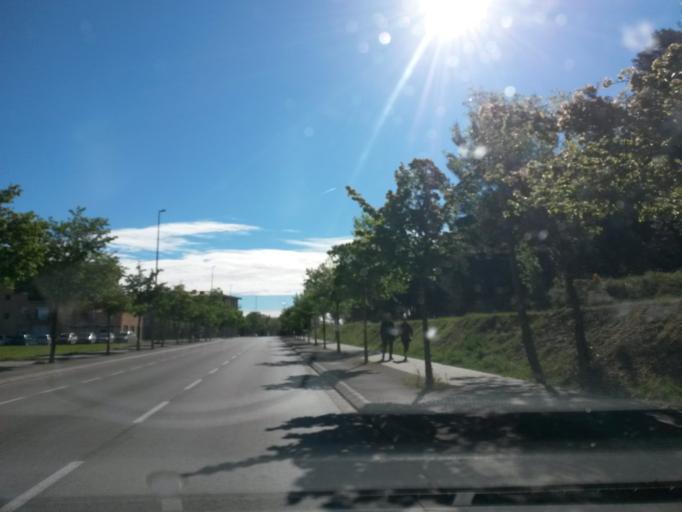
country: ES
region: Catalonia
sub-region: Provincia de Girona
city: Celra
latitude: 42.0266
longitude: 2.8880
